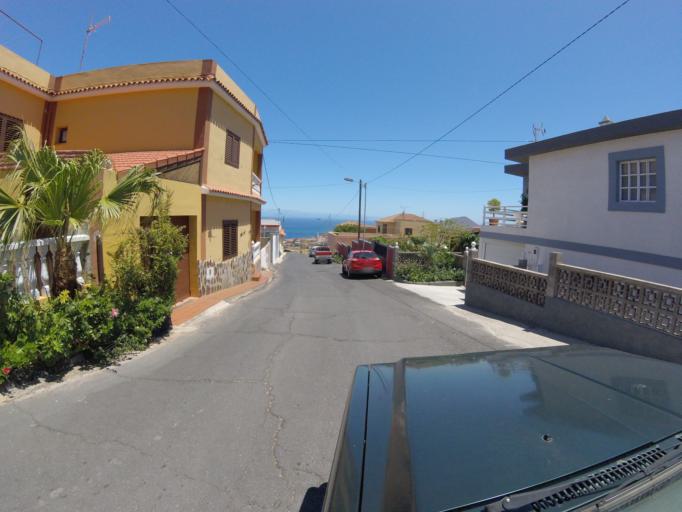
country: ES
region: Canary Islands
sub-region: Provincia de Santa Cruz de Tenerife
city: Candelaria
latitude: 28.3652
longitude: -16.3783
